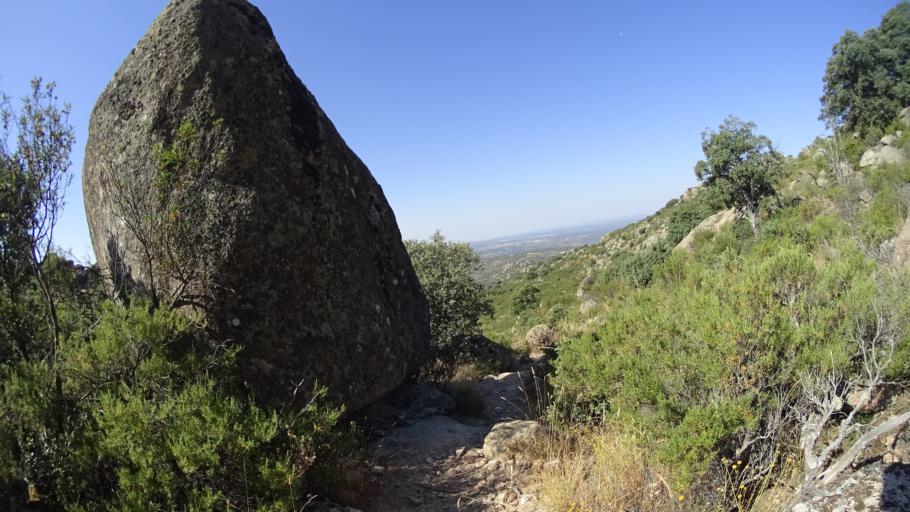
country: ES
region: Madrid
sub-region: Provincia de Madrid
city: Hoyo de Manzanares
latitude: 40.6458
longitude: -3.9342
